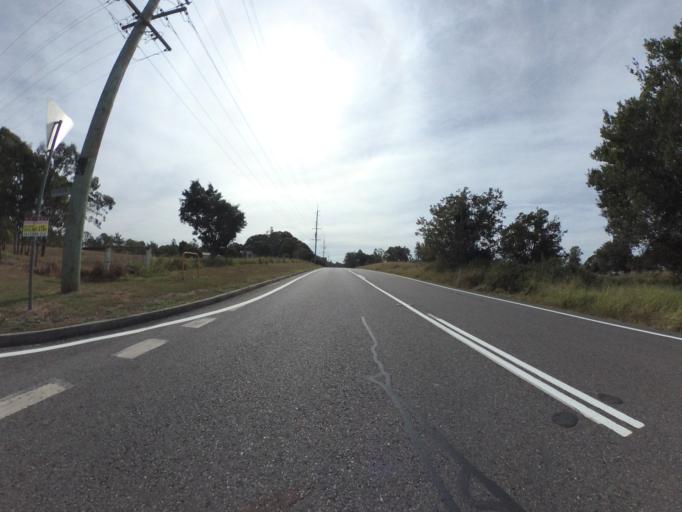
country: AU
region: Queensland
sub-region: Brisbane
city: Moggill
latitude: -27.5860
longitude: 152.8613
